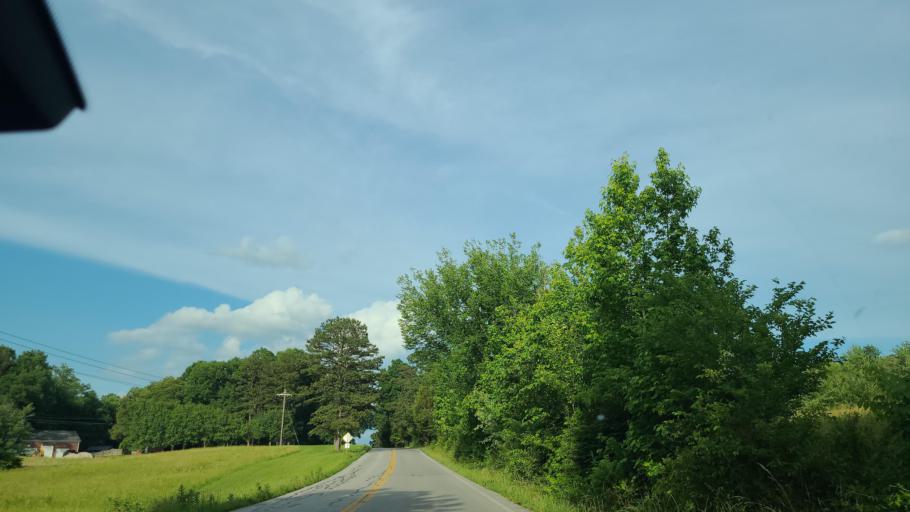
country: US
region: Kentucky
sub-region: Whitley County
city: Corbin
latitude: 36.8821
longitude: -84.2071
